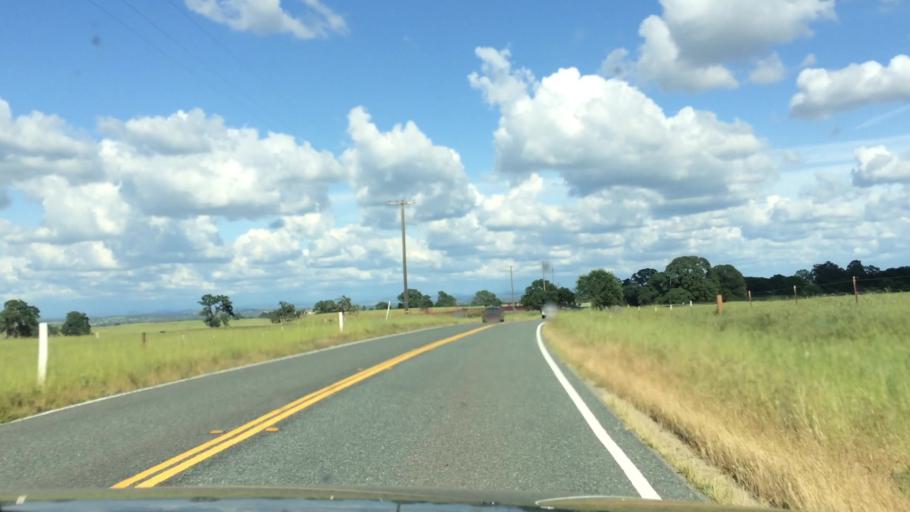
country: US
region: California
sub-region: Amador County
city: Ione
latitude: 38.3859
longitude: -121.0479
